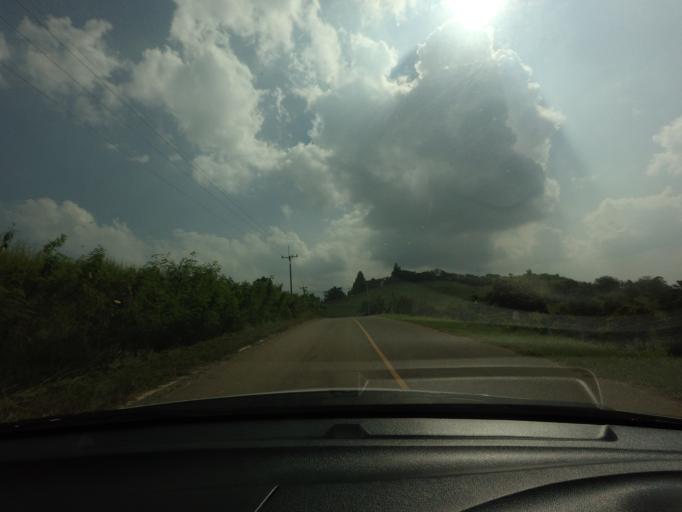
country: TH
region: Nakhon Ratchasima
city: Pak Chong
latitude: 14.5219
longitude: 101.5738
